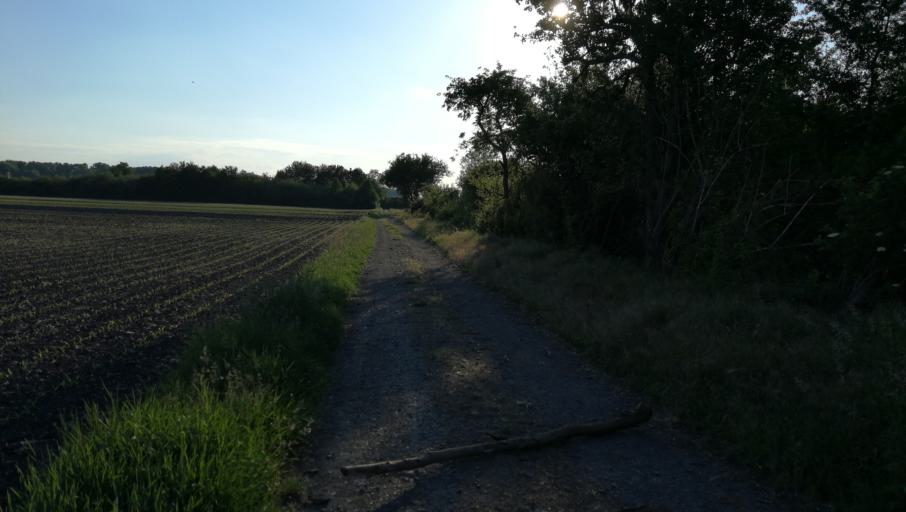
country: DE
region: Baden-Wuerttemberg
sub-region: Karlsruhe Region
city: Altlussheim
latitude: 49.3174
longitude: 8.4806
